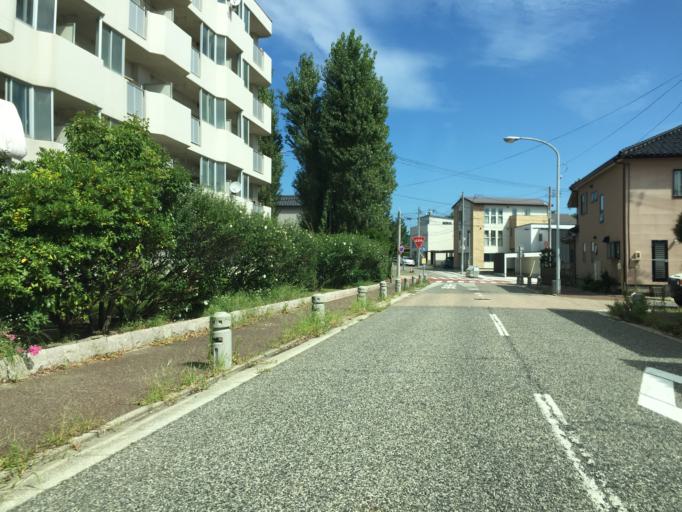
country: JP
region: Niigata
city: Niigata-shi
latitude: 37.9394
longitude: 139.0555
